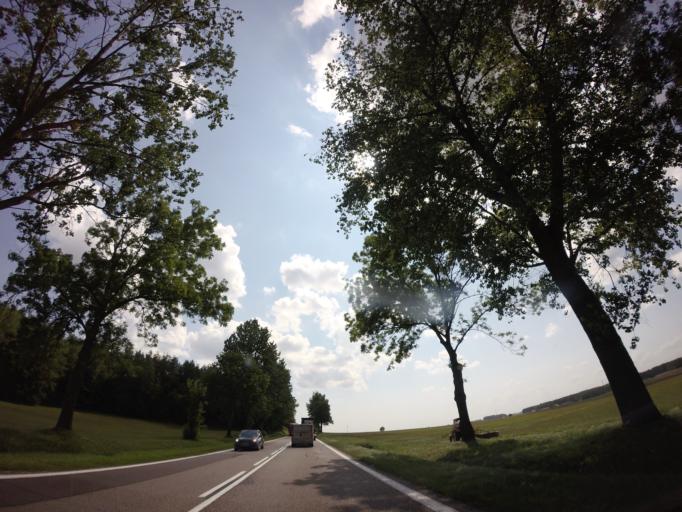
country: PL
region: Podlasie
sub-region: Powiat lomzynski
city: Piatnica
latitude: 53.2685
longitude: 22.1301
